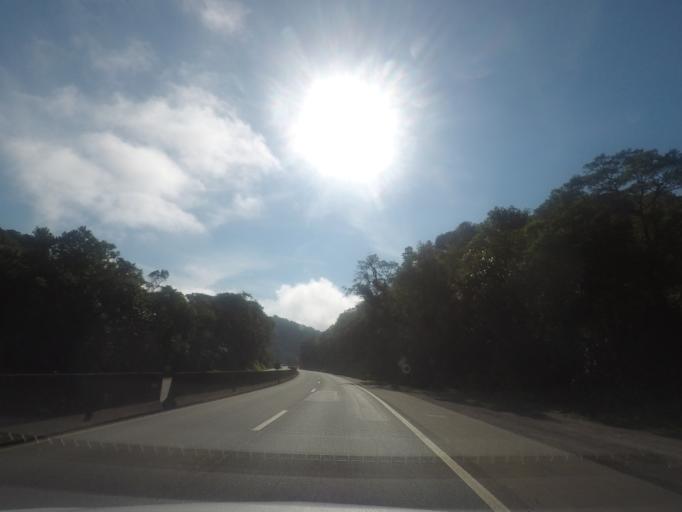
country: BR
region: Parana
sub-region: Piraquara
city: Piraquara
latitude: -25.5953
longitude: -48.8979
